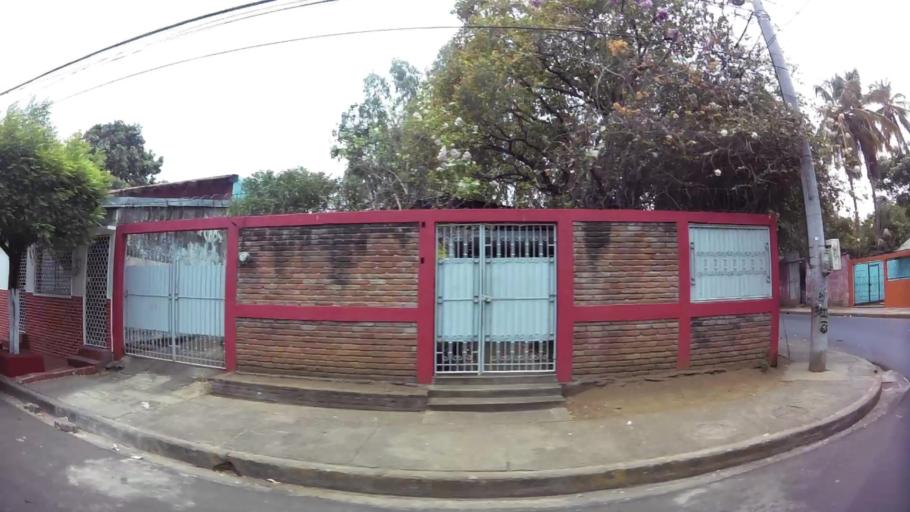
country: NI
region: Managua
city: Managua
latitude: 12.1338
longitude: -86.2947
